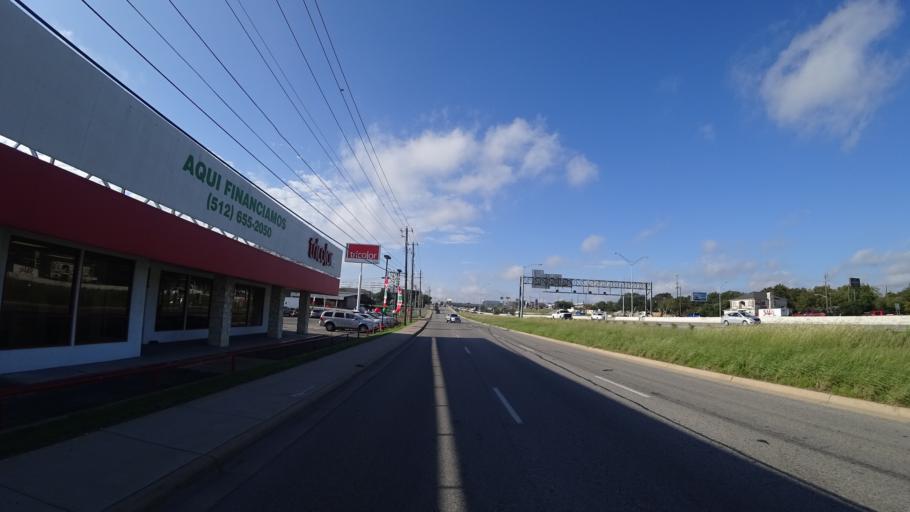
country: US
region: Texas
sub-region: Travis County
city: Austin
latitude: 30.3356
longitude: -97.7018
